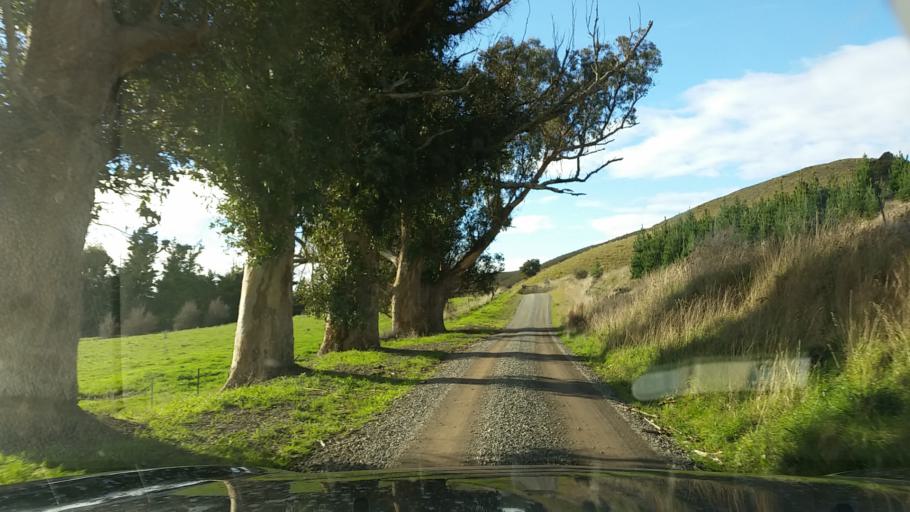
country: NZ
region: Marlborough
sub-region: Marlborough District
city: Blenheim
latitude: -41.7756
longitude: 173.8534
